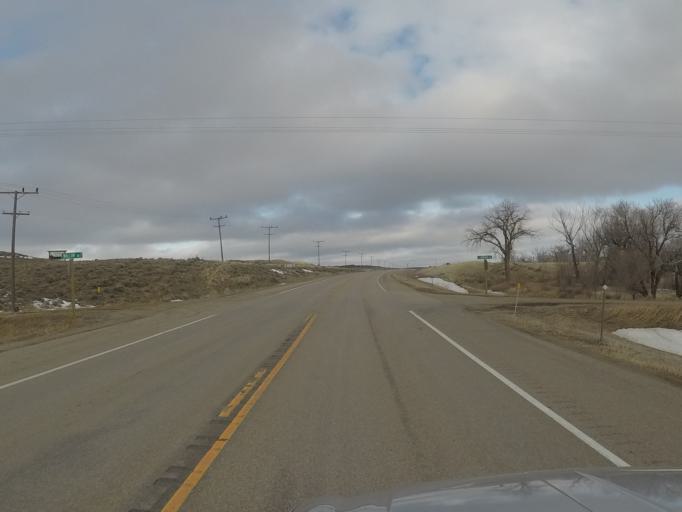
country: US
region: Montana
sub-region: Golden Valley County
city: Ryegate
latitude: 46.3149
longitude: -109.3843
